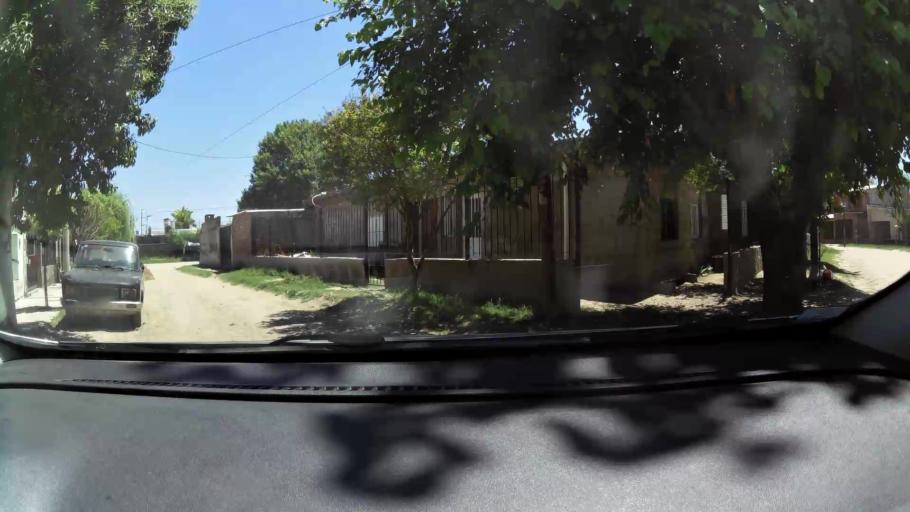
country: AR
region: Cordoba
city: Malvinas Argentinas
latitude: -31.4287
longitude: -64.1110
